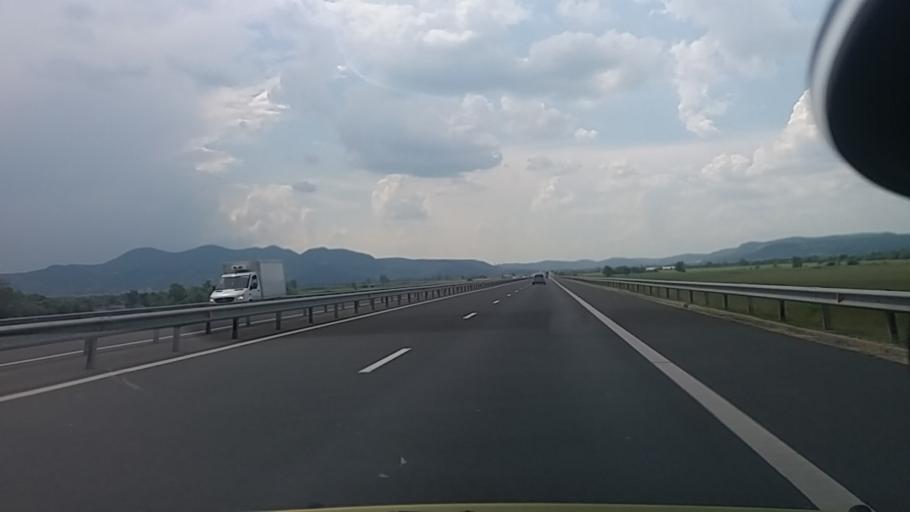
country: RO
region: Hunedoara
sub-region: Comuna Harau
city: Harau
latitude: 45.8886
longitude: 22.9713
